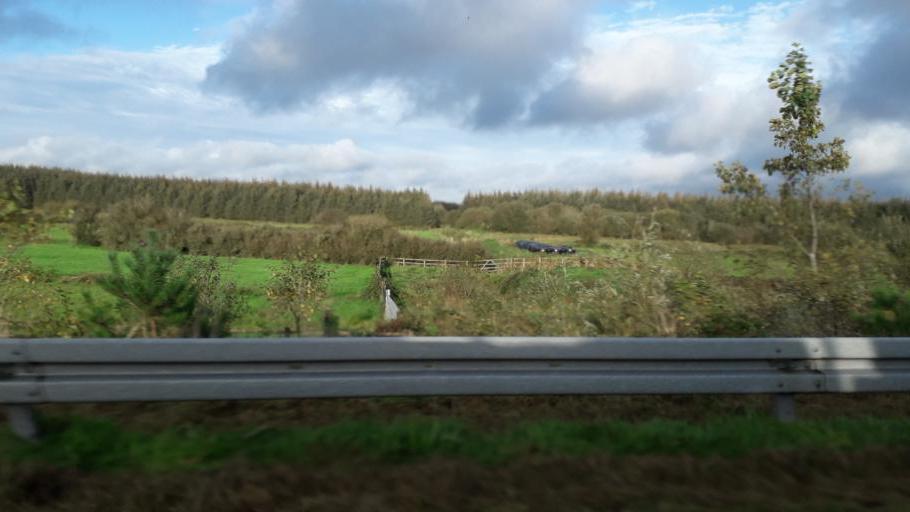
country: IE
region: Connaught
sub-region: Roscommon
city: Ballaghaderreen
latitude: 53.9088
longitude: -8.5484
